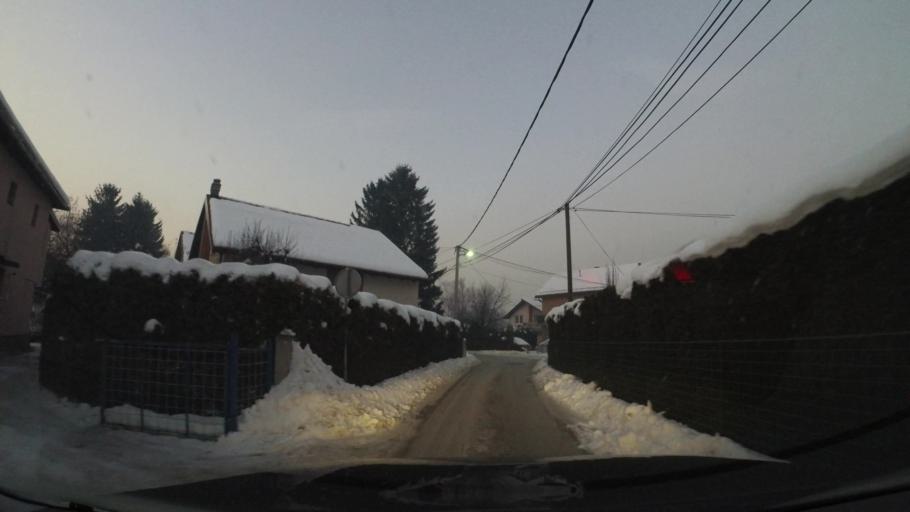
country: BA
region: Federation of Bosnia and Herzegovina
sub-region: Kanton Sarajevo
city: Sarajevo
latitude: 43.8351
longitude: 18.3214
